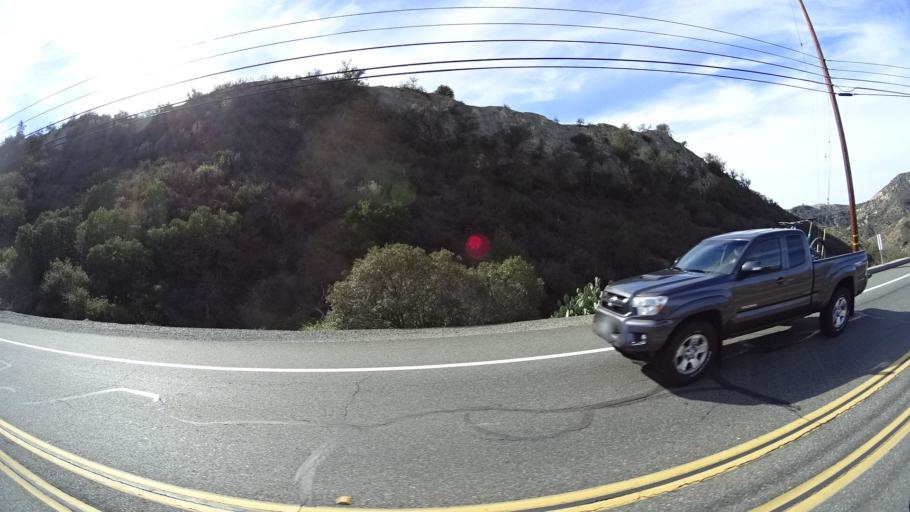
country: US
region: California
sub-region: Orange County
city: Portola Hills
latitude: 33.6996
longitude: -117.6392
